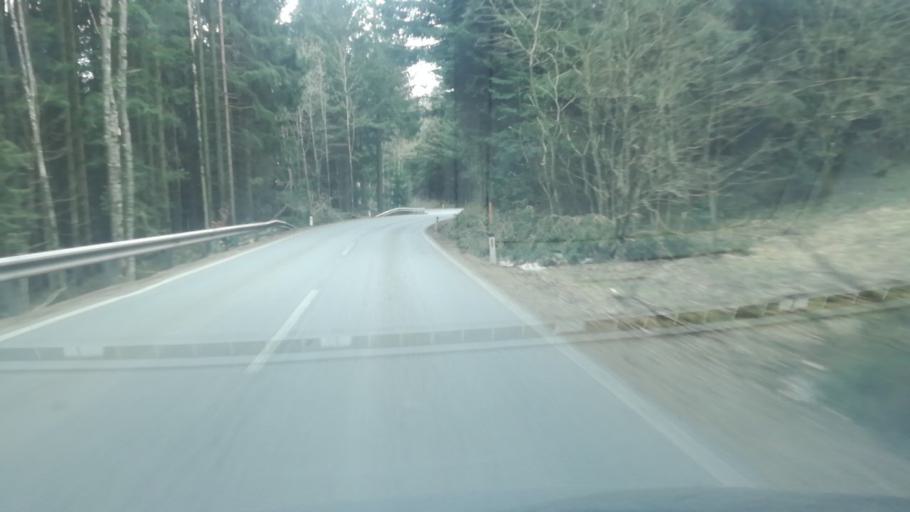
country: AT
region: Upper Austria
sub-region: Politischer Bezirk Vocklabruck
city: Frankenburg
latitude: 48.1144
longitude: 13.4804
